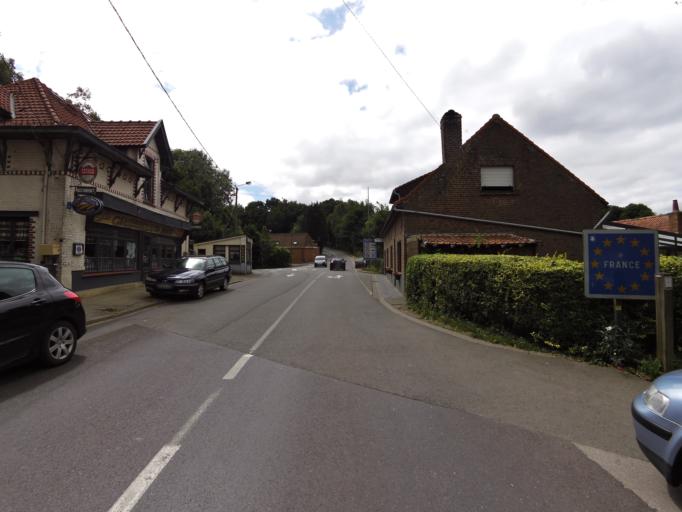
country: FR
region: Nord-Pas-de-Calais
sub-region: Departement du Nord
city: Saint-Jans-Cappel
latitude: 50.7805
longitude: 2.7385
